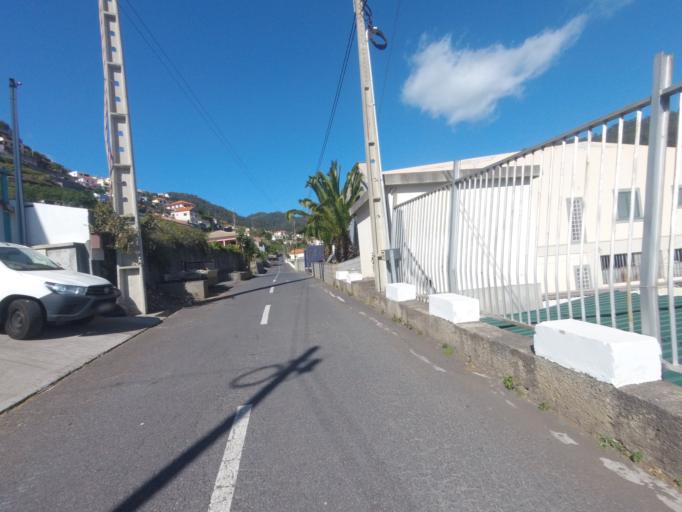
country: PT
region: Madeira
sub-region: Ribeira Brava
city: Campanario
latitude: 32.6744
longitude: -17.0292
